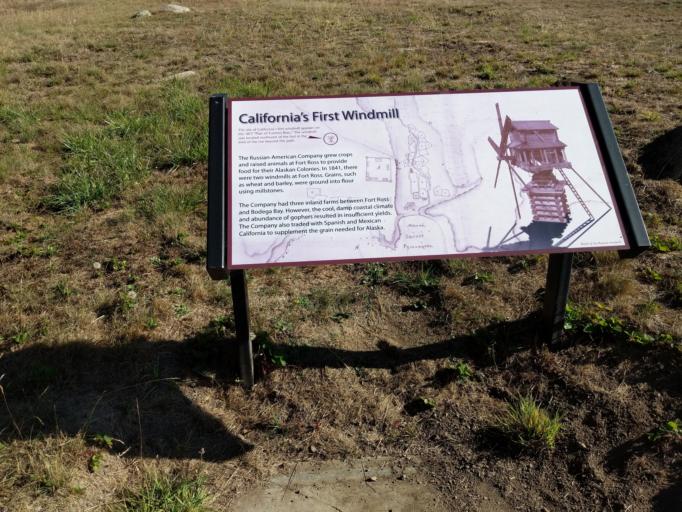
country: US
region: California
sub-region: Sonoma County
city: Monte Rio
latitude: 38.5156
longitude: -123.2452
